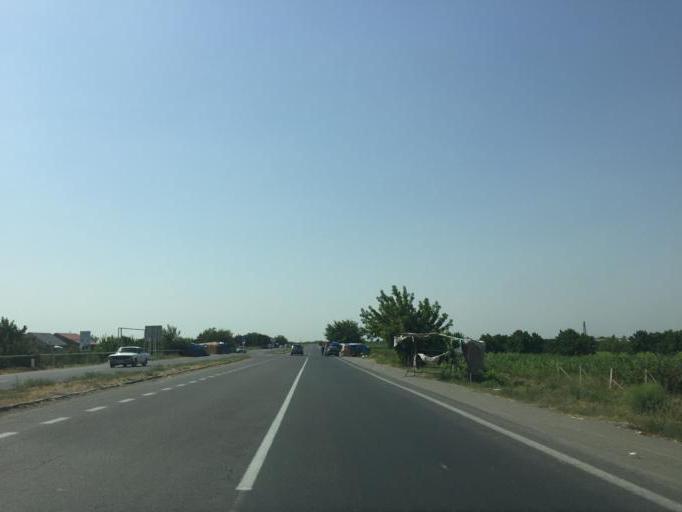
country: AM
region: Ararat
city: Aralez
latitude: 39.9082
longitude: 44.6057
